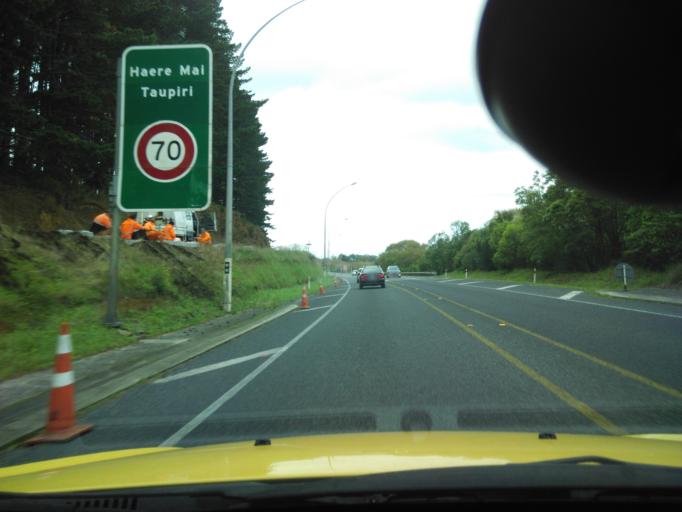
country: NZ
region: Waikato
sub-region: Waikato District
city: Ngaruawahia
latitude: -37.6064
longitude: 175.1789
